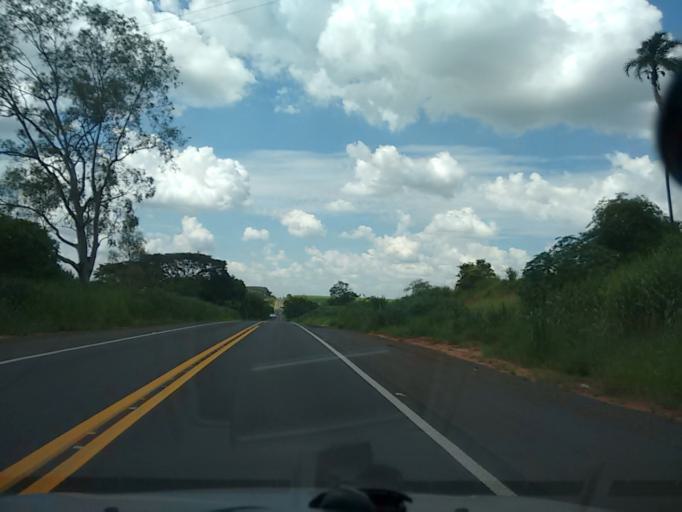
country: BR
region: Sao Paulo
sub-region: Osvaldo Cruz
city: Osvaldo Cruz
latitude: -21.8441
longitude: -50.8309
